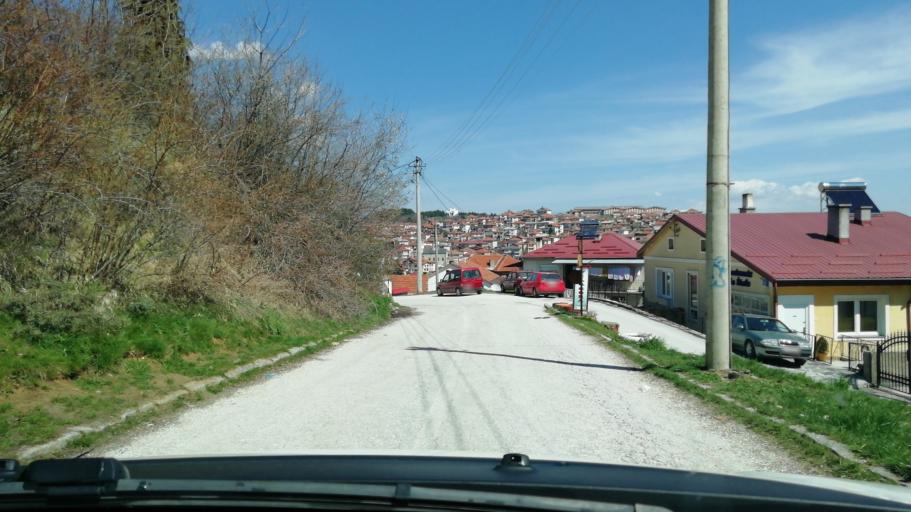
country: MK
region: Krusevo
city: Krushevo
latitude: 41.3651
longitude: 21.2502
